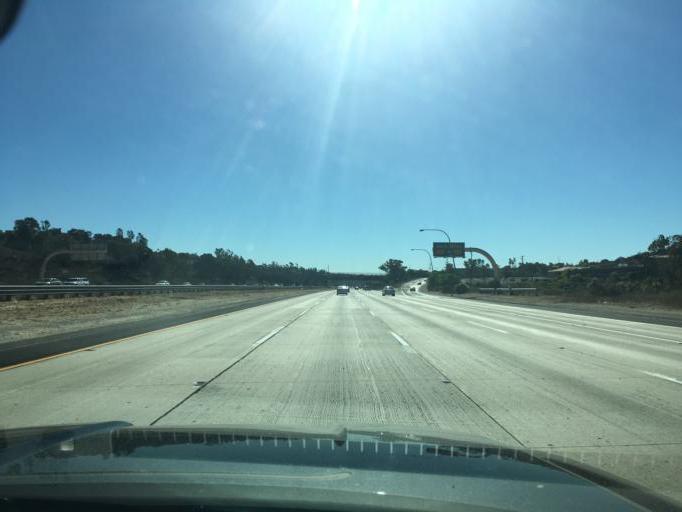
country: US
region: California
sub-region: San Diego County
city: La Mesa
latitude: 32.8144
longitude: -117.1148
